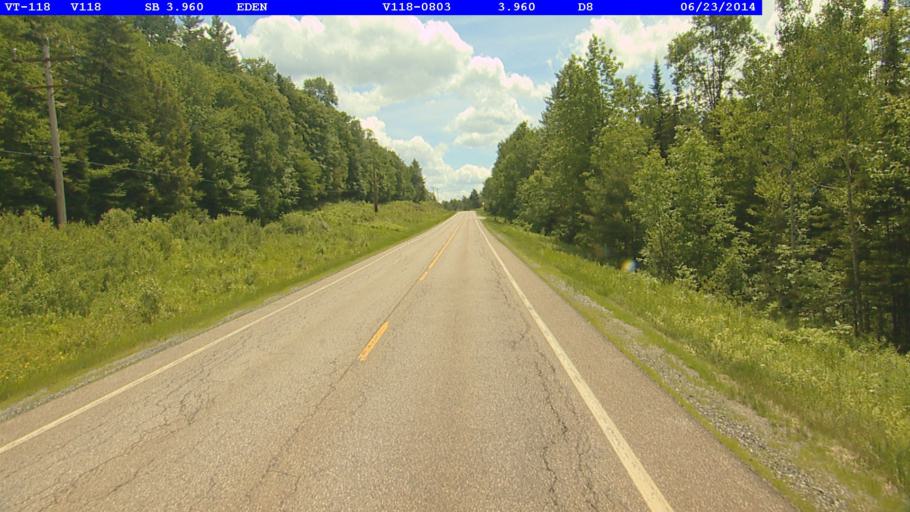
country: US
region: Vermont
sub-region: Lamoille County
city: Johnson
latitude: 44.7562
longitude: -72.5805
